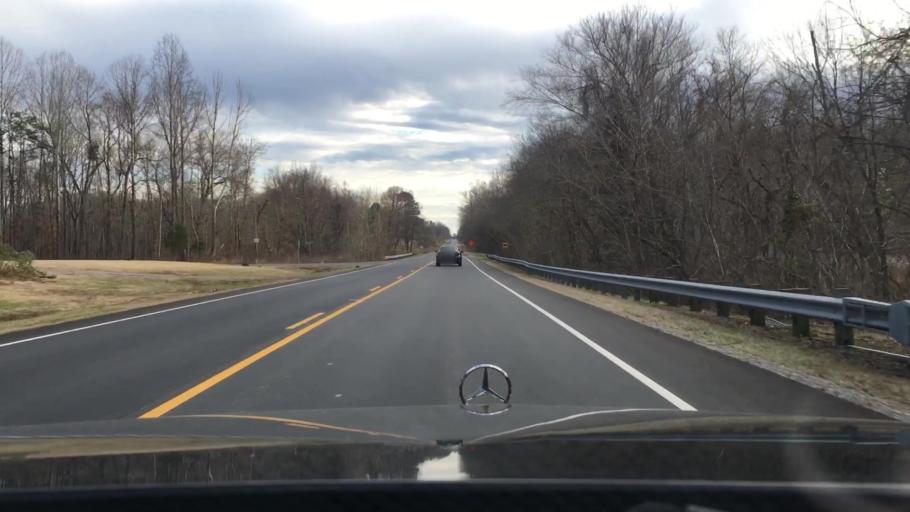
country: US
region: North Carolina
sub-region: Caswell County
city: Yanceyville
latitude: 36.4656
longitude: -79.3743
